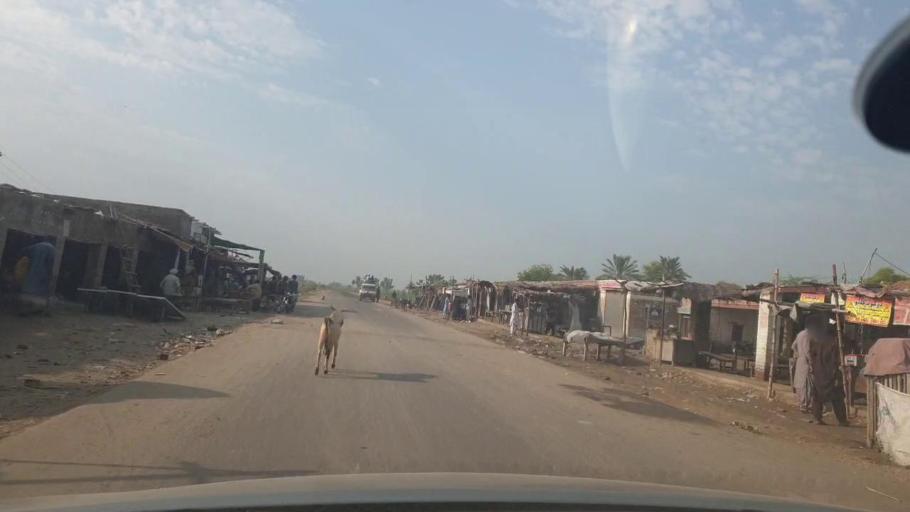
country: PK
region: Sindh
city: Jacobabad
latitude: 28.1058
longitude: 68.3261
